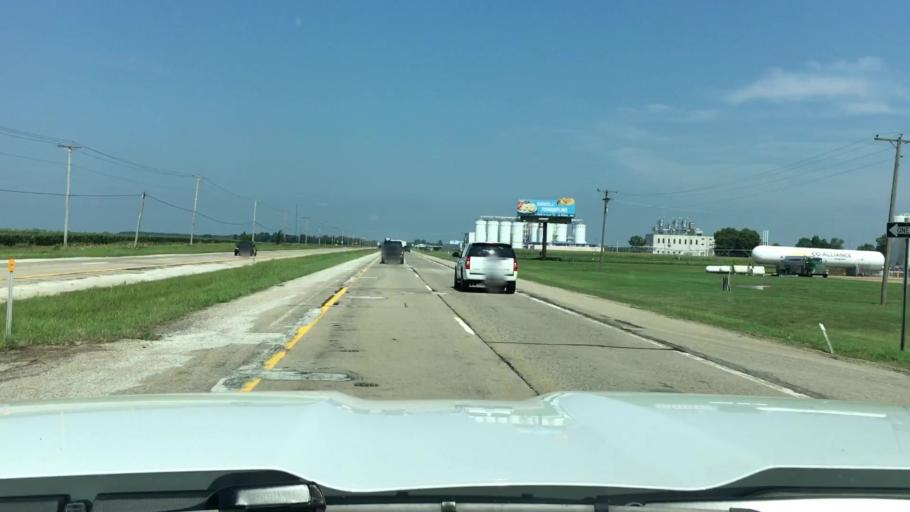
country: US
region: Michigan
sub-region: Kalamazoo County
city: Schoolcraft
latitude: 42.0738
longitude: -85.6365
